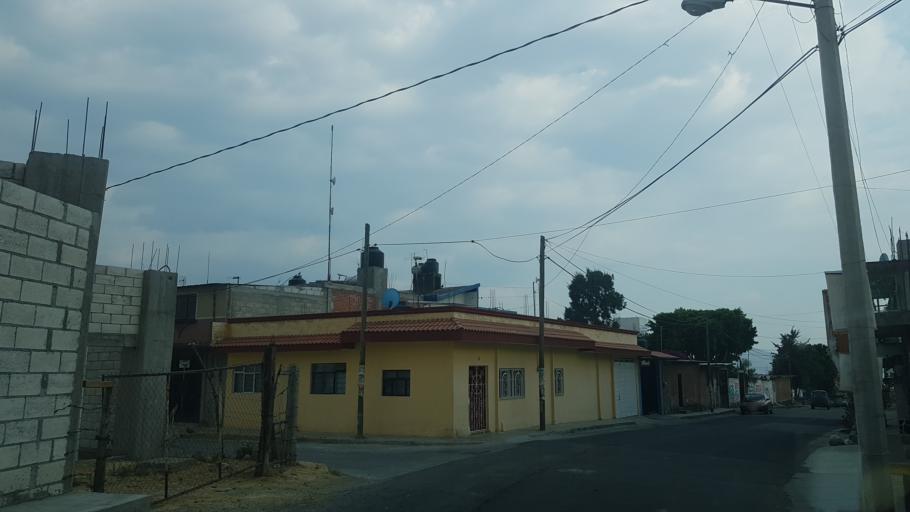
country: MX
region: Puebla
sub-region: Santa Isabel Cholula
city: Santa Ana Acozautla
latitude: 18.9482
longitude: -98.3951
